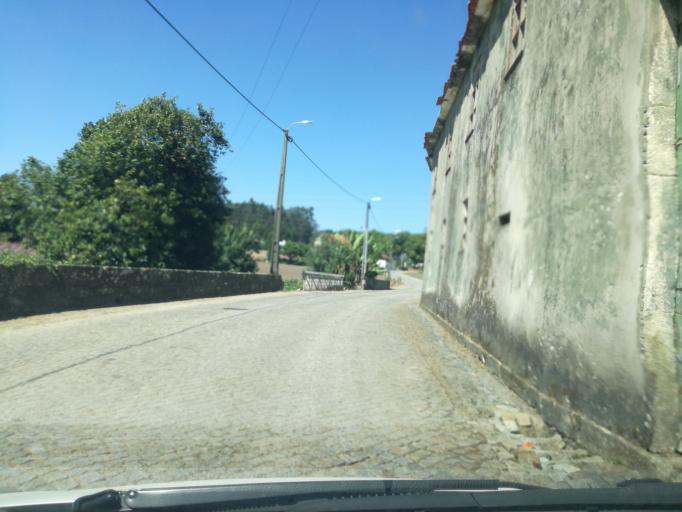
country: PT
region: Porto
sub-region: Maia
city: Gemunde
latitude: 41.2729
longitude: -8.6388
